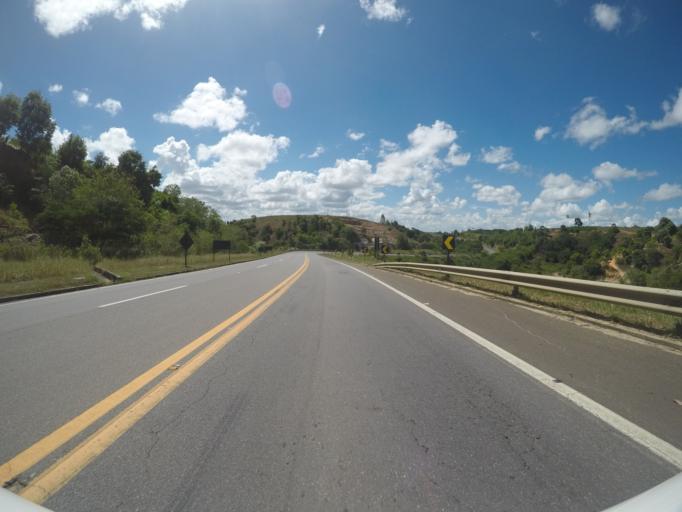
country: BR
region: Espirito Santo
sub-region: Conceicao Da Barra
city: Conceicao da Barra
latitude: -18.2859
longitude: -39.9552
